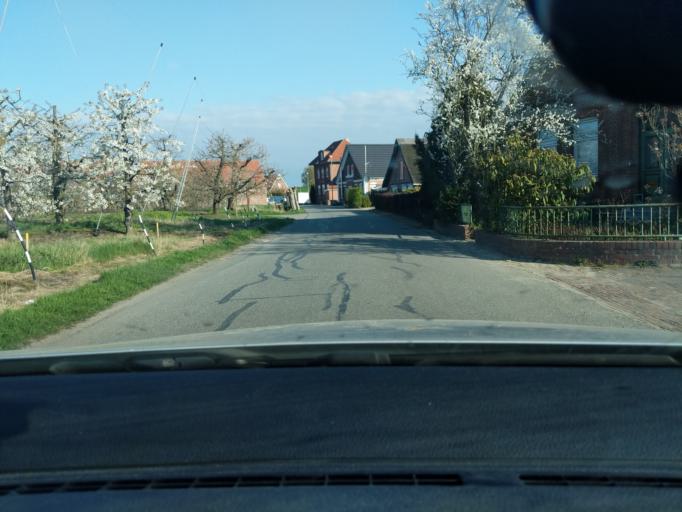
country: DE
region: Lower Saxony
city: Grunendeich
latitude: 53.5675
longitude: 9.6400
